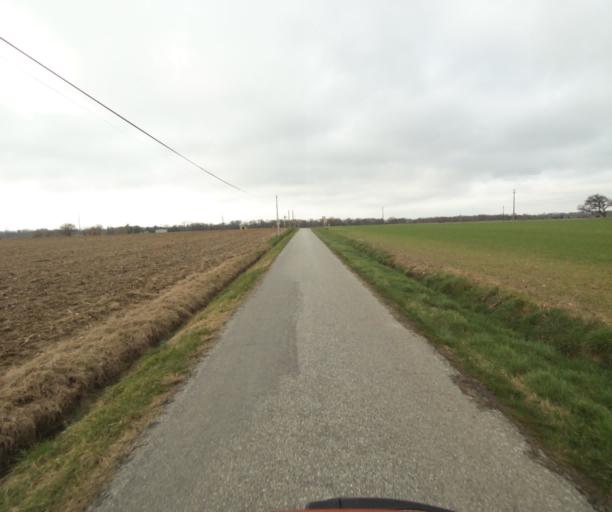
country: FR
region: Languedoc-Roussillon
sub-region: Departement de l'Aude
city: Belpech
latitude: 43.1804
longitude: 1.7135
